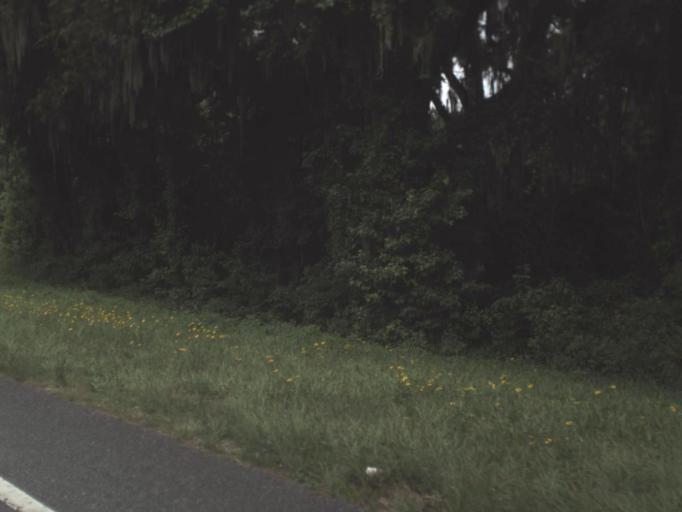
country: US
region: Florida
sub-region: Suwannee County
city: Live Oak
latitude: 30.3505
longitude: -82.9480
